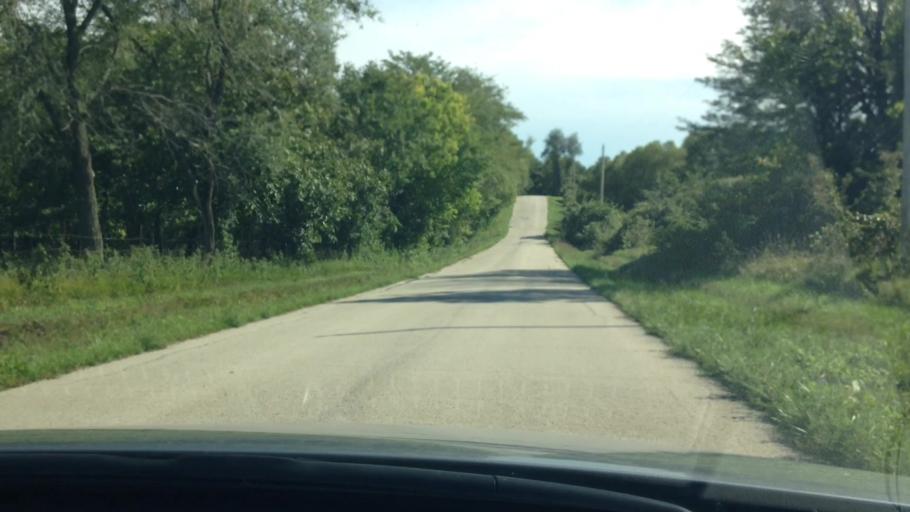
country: US
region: Missouri
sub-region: Clay County
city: Smithville
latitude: 39.3350
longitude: -94.6675
